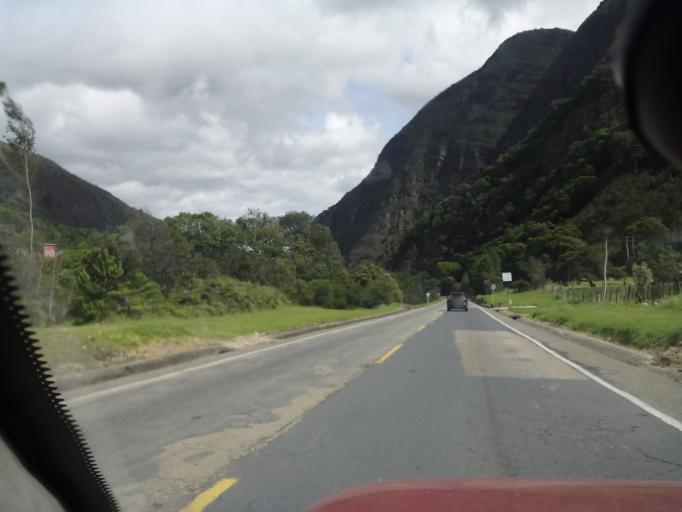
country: CO
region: Boyaca
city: Arcabuco
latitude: 5.7423
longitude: -73.4210
